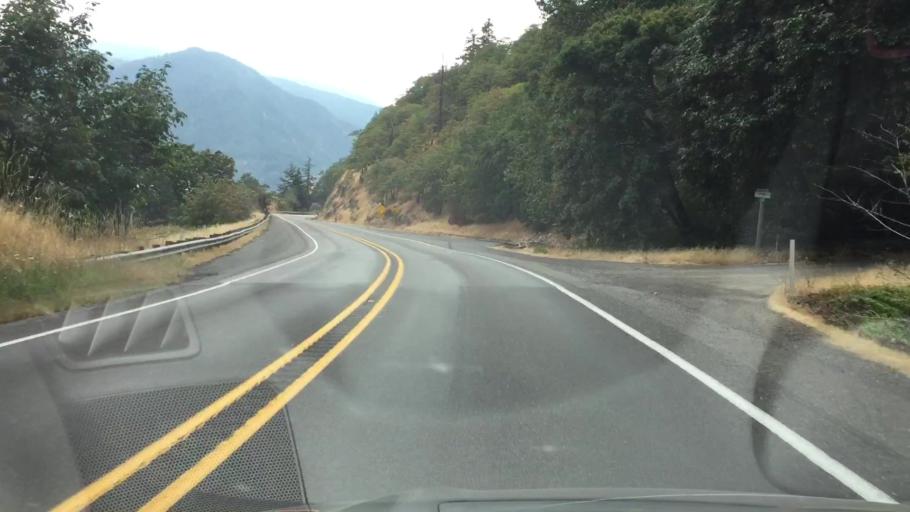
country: US
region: Oregon
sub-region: Hood River County
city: Hood River
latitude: 45.7207
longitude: -121.6051
